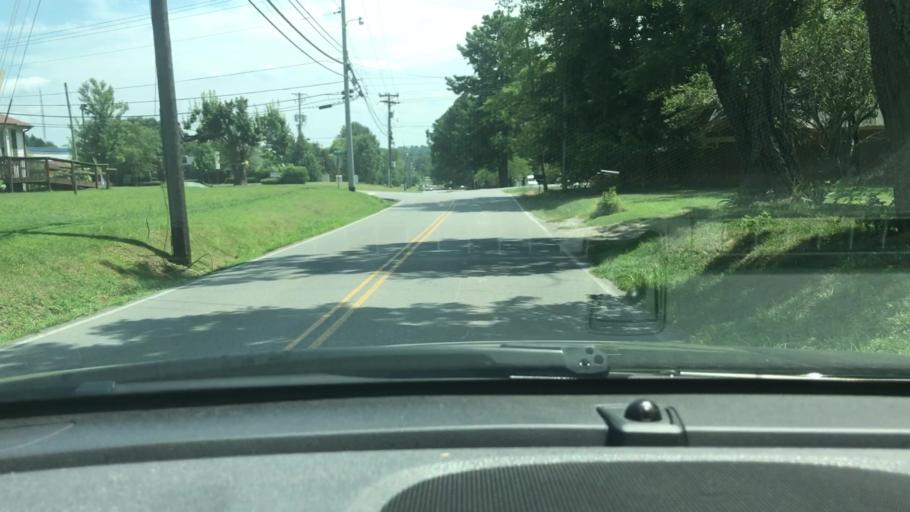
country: US
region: Tennessee
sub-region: Sumner County
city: White House
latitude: 36.4668
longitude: -86.6489
